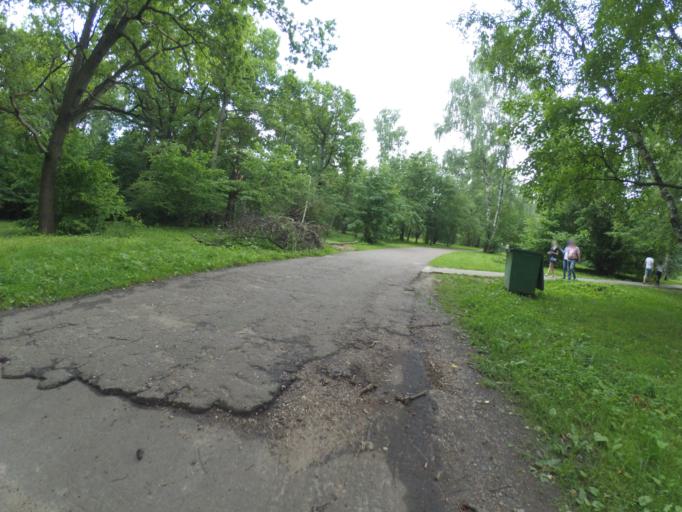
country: RU
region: Moscow
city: Novovladykino
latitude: 55.8447
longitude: 37.5931
